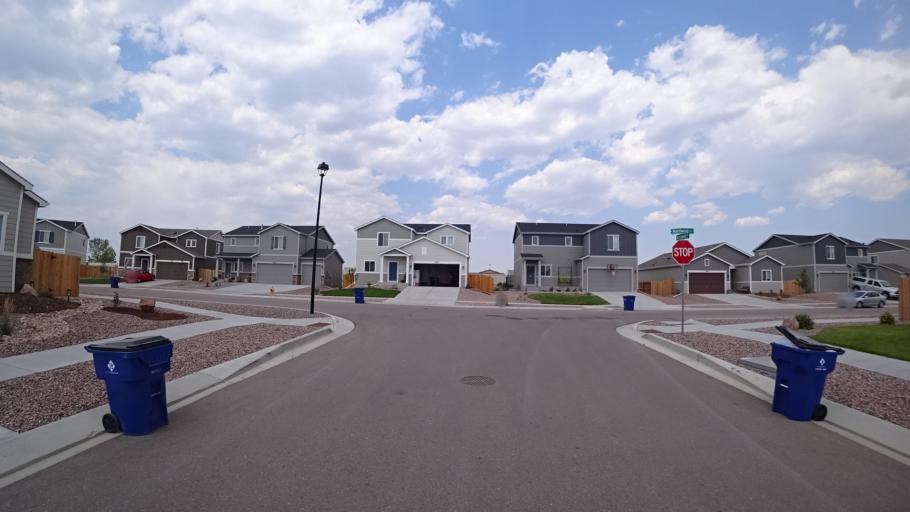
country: US
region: Colorado
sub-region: El Paso County
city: Black Forest
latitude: 38.9474
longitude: -104.6878
